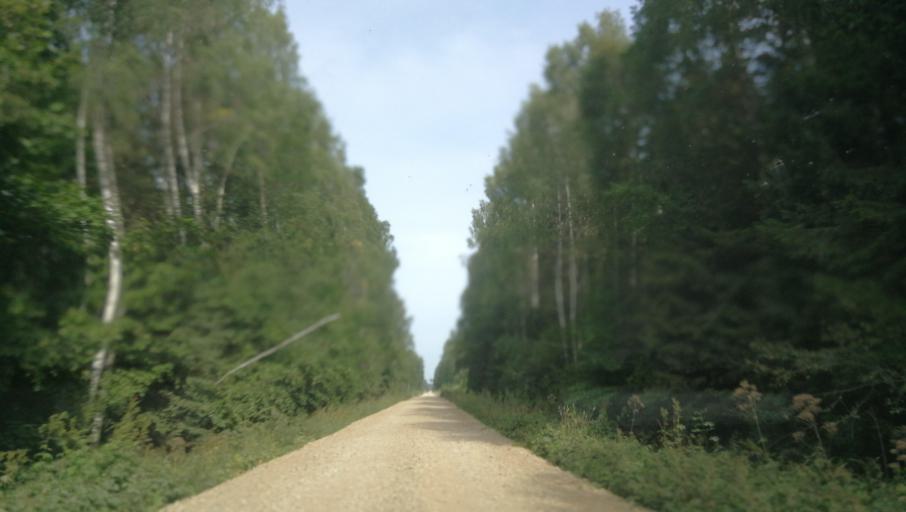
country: LV
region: Durbe
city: Liegi
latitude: 56.7537
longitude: 21.3578
